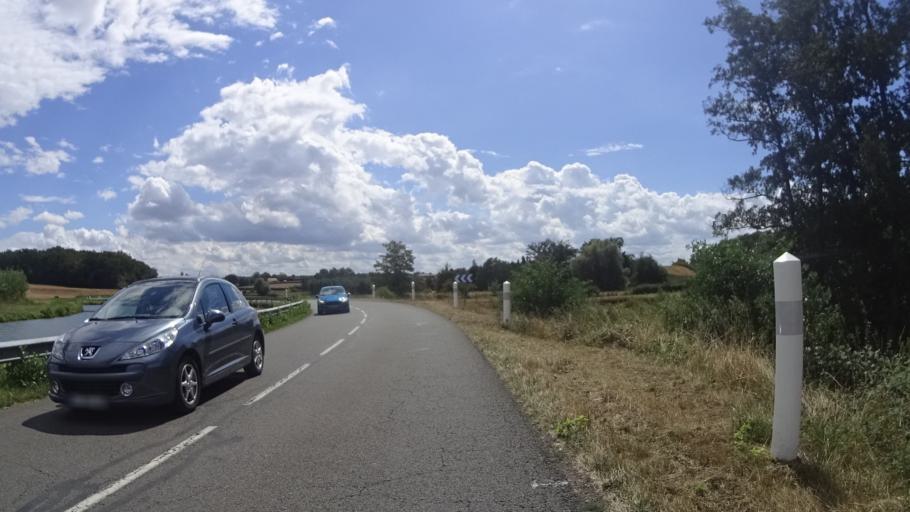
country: FR
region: Bourgogne
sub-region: Departement de Saone-et-Loire
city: Saint-Vallier
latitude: 46.6304
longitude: 4.3325
